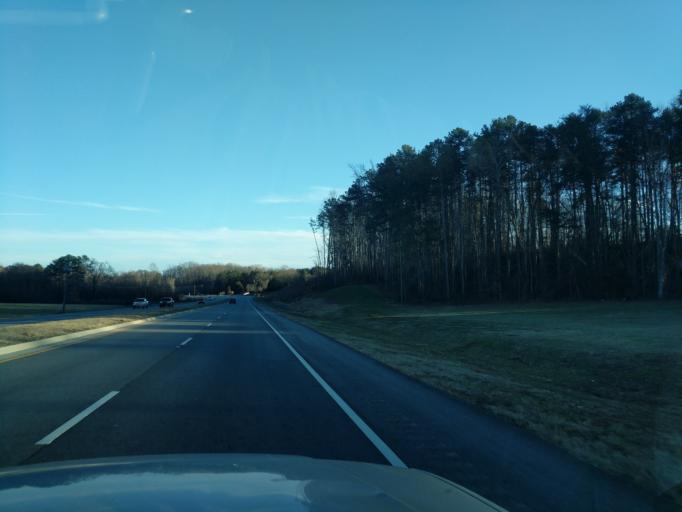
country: US
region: Georgia
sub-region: Stephens County
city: Toccoa
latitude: 34.5393
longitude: -83.2665
